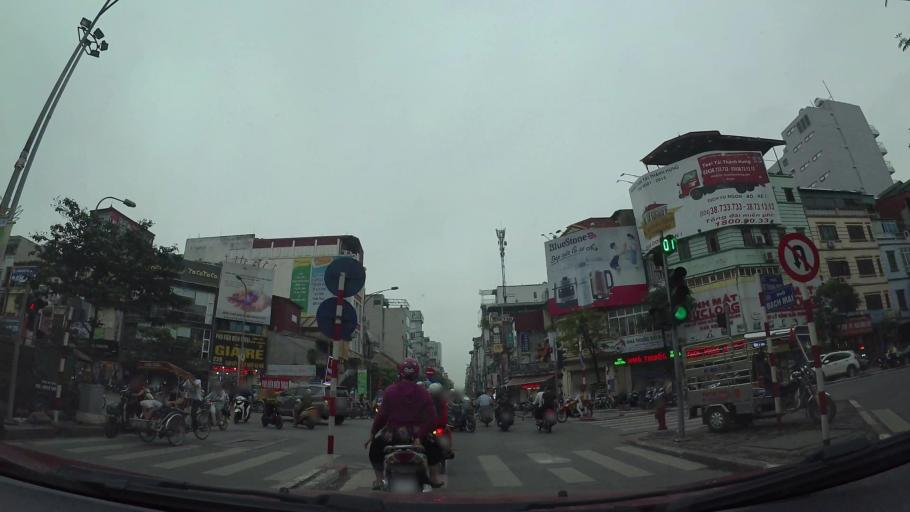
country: VN
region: Ha Noi
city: Hai BaTrung
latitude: 21.0033
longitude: 105.8510
